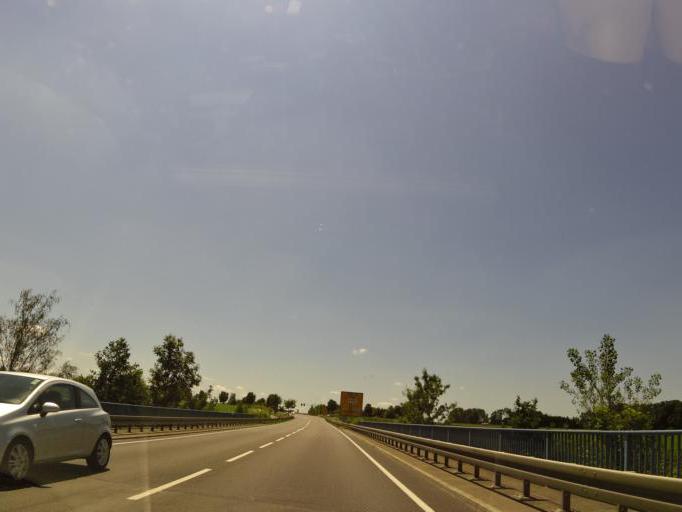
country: DE
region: Bavaria
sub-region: Swabia
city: Guenzburg
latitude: 48.4420
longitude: 10.2889
